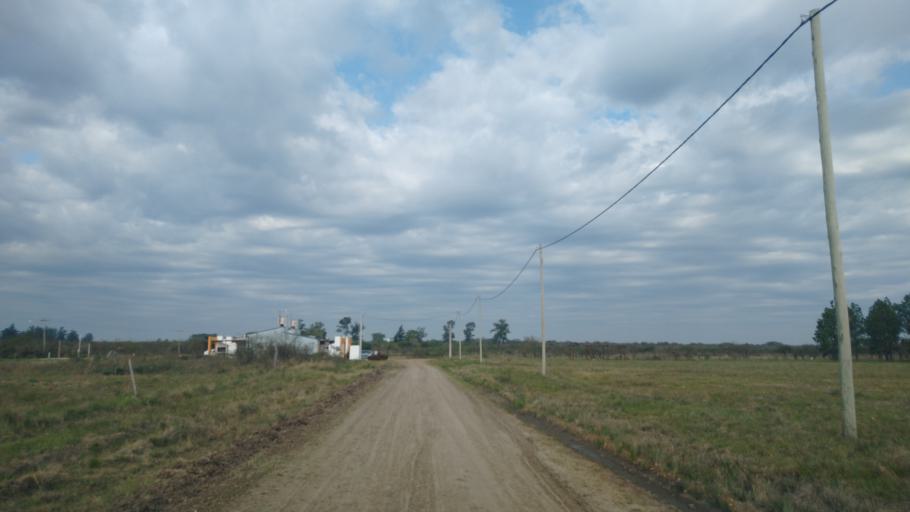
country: AR
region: Entre Rios
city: Chajari
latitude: -30.7430
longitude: -58.0090
